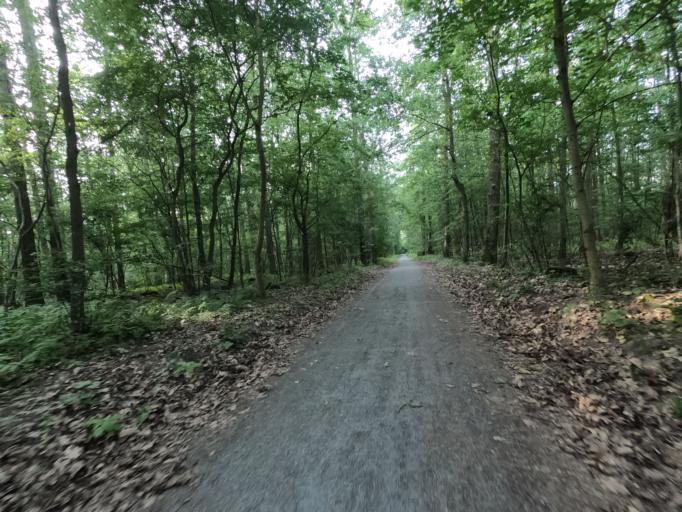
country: DE
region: Hesse
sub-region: Regierungsbezirk Darmstadt
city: Russelsheim
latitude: 49.9678
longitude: 8.4155
